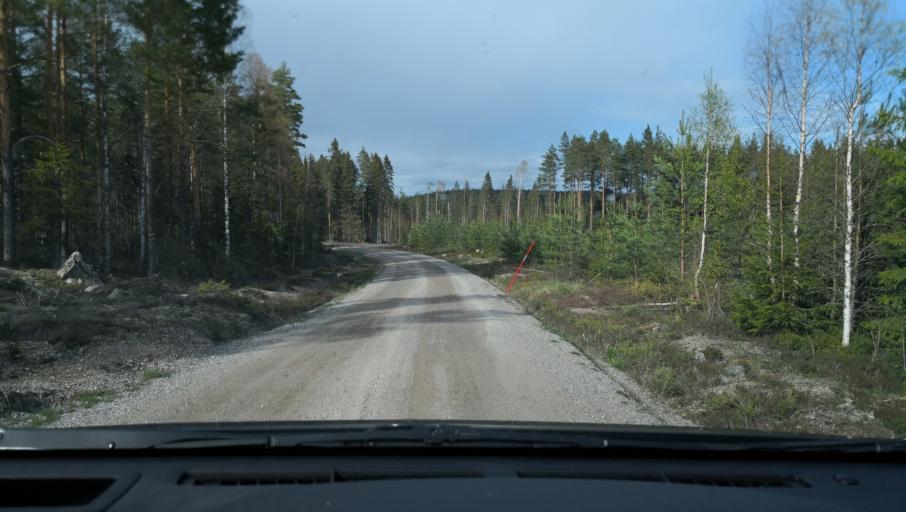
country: SE
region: Dalarna
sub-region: Saters Kommun
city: Saeter
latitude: 60.1700
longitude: 15.7201
